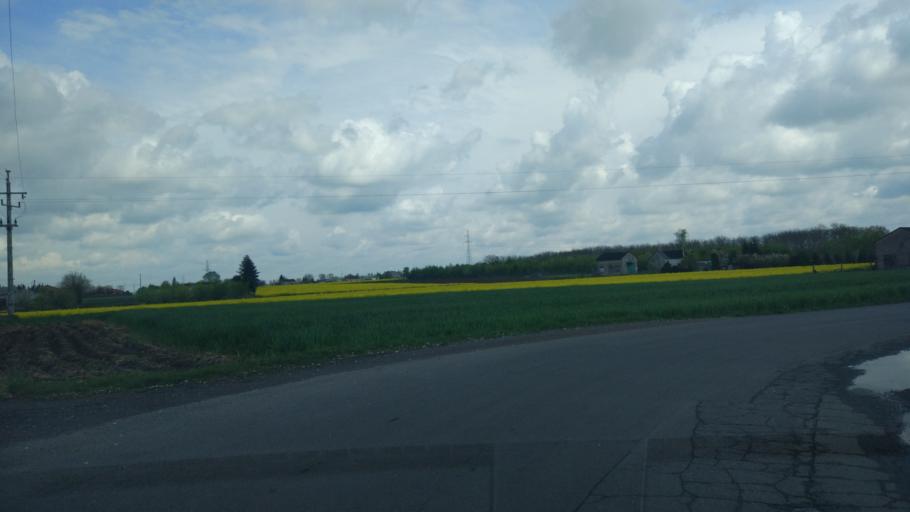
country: PL
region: Lodz Voivodeship
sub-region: Powiat kutnowski
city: Kutno
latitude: 52.2312
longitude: 19.4061
